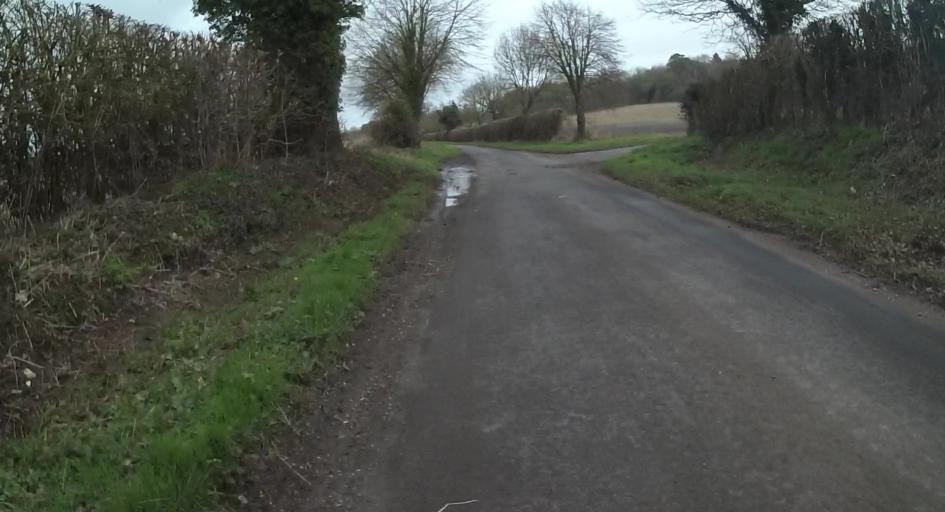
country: GB
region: England
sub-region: Hampshire
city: Overton
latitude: 51.2647
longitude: -1.1969
